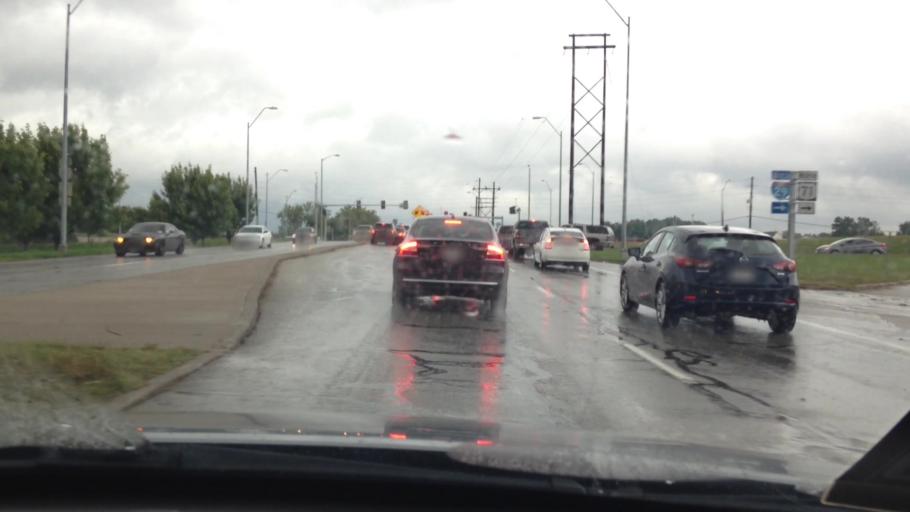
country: US
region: Missouri
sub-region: Clay County
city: Gladstone
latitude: 39.1799
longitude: -94.5766
